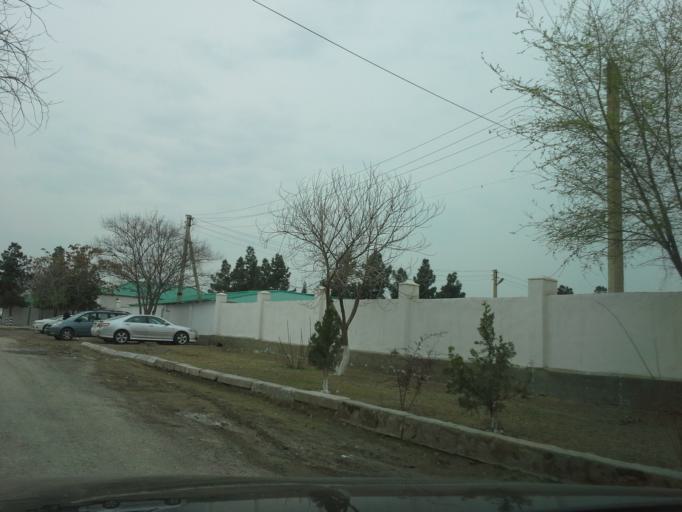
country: TM
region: Ahal
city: Ashgabat
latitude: 37.9594
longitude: 58.3435
